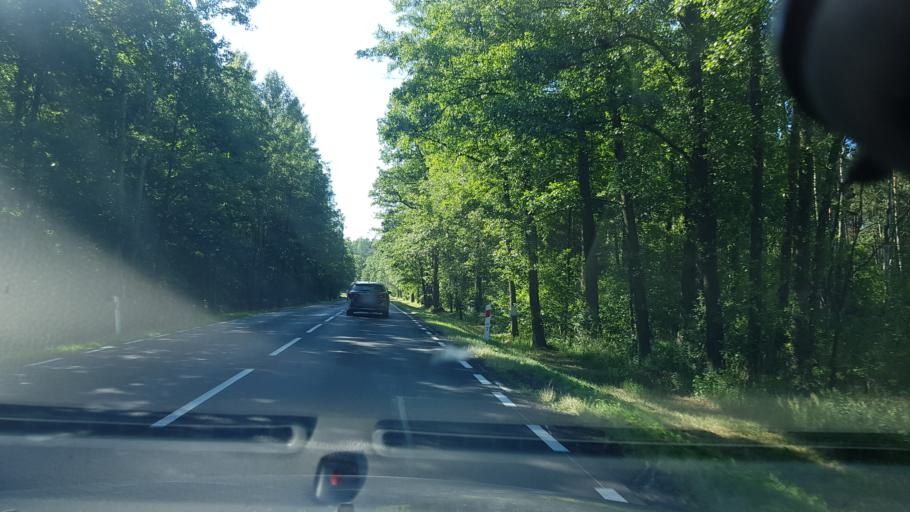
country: PL
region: Masovian Voivodeship
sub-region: Powiat wyszkowski
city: Branszczyk
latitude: 52.5717
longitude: 21.5417
